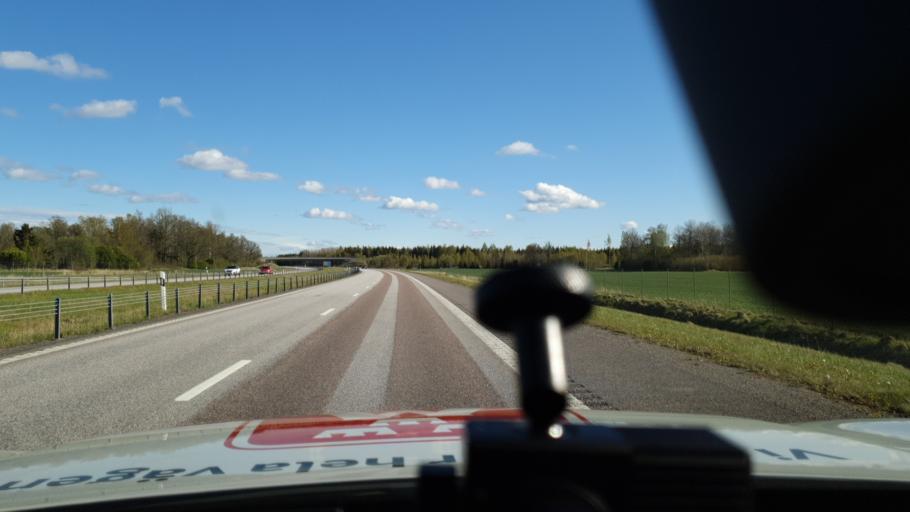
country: SE
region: Uppsala
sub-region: Osthammars Kommun
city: Bjorklinge
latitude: 60.0591
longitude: 17.6151
